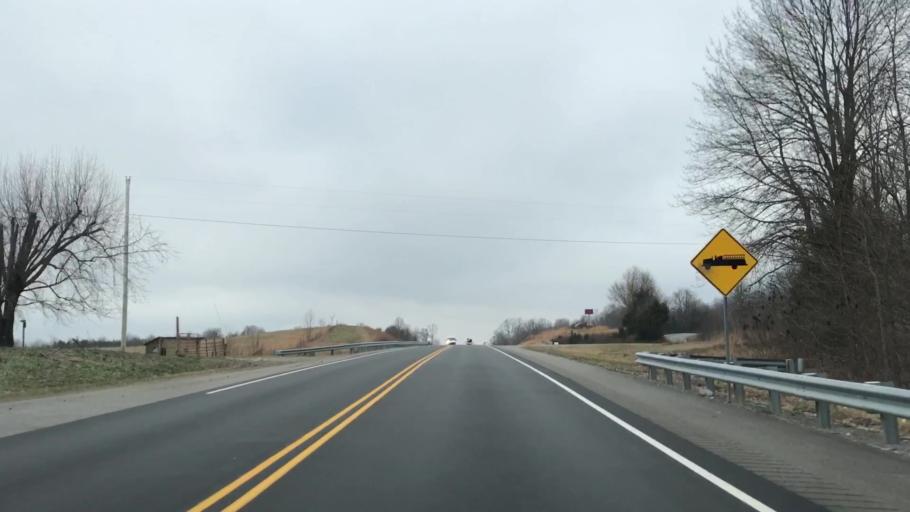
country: US
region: Kentucky
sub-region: Adair County
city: Columbia
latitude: 36.9702
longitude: -85.4273
